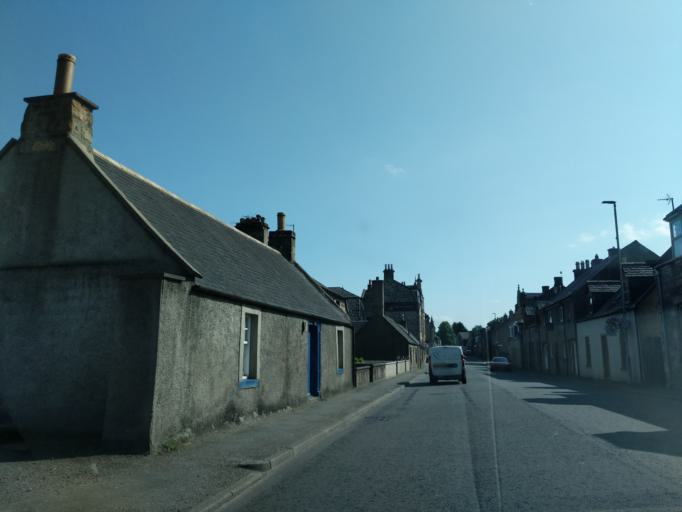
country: GB
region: Scotland
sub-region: Moray
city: Rothes
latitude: 57.5298
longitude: -3.2081
